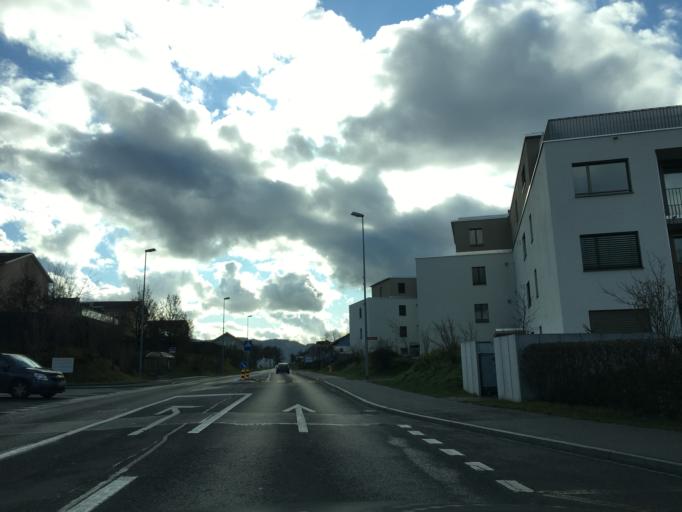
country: CH
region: Aargau
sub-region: Bezirk Muri
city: Oberruti
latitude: 47.1654
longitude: 8.3944
